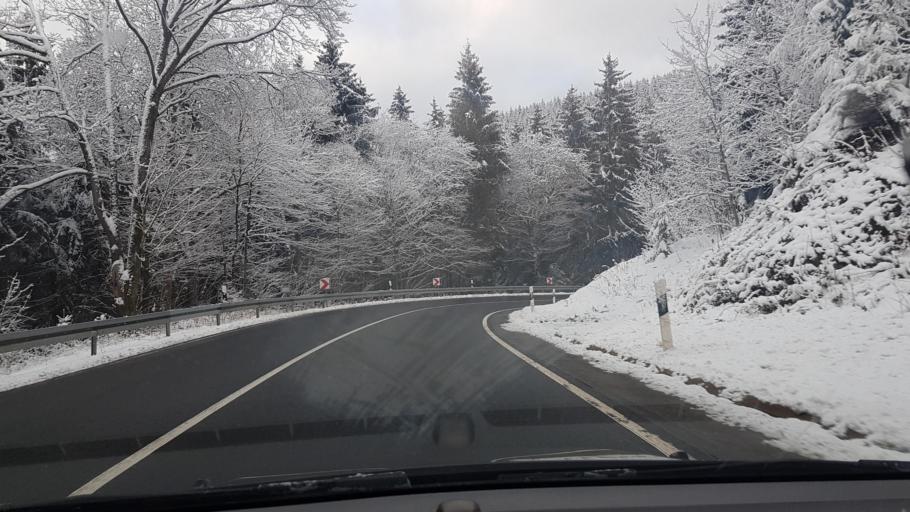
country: DE
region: Lower Saxony
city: Wildemann
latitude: 51.8090
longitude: 10.2638
